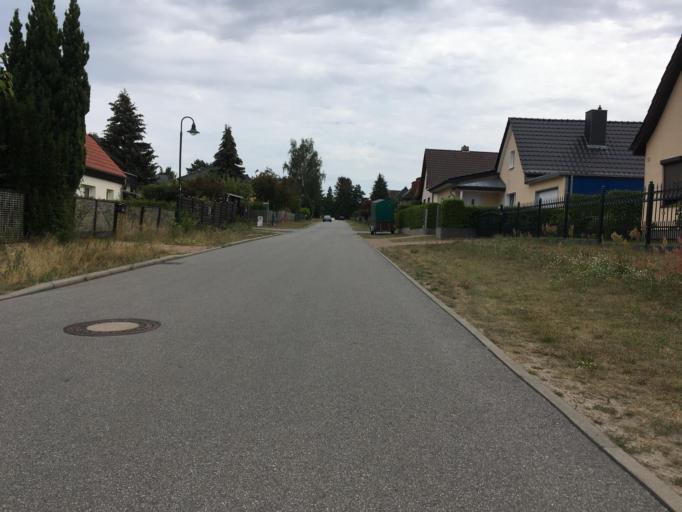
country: DE
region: Berlin
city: Buch
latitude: 52.6453
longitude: 13.5305
